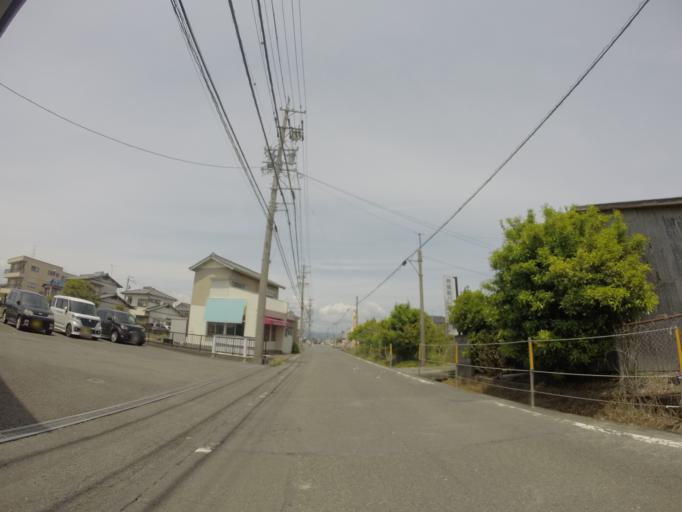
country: JP
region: Shizuoka
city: Yaizu
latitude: 34.8409
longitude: 138.2944
